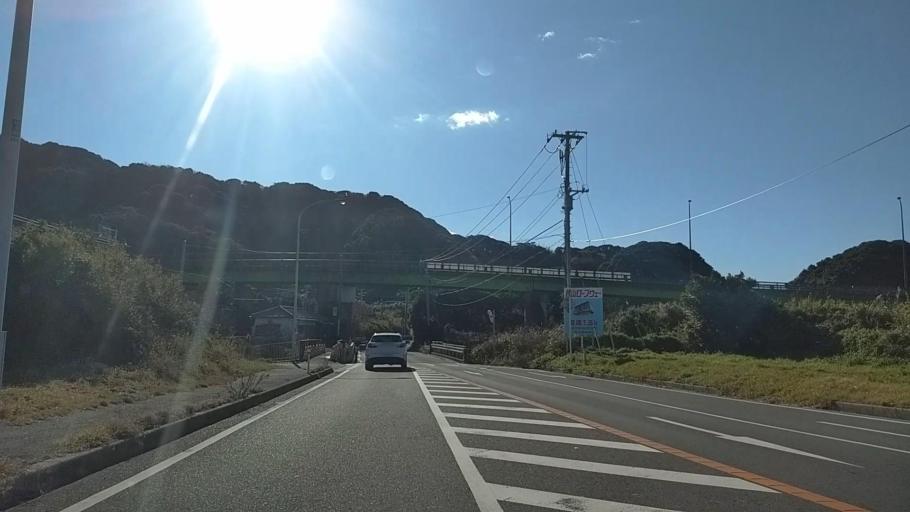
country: JP
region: Chiba
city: Futtsu
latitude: 35.1747
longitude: 139.8190
